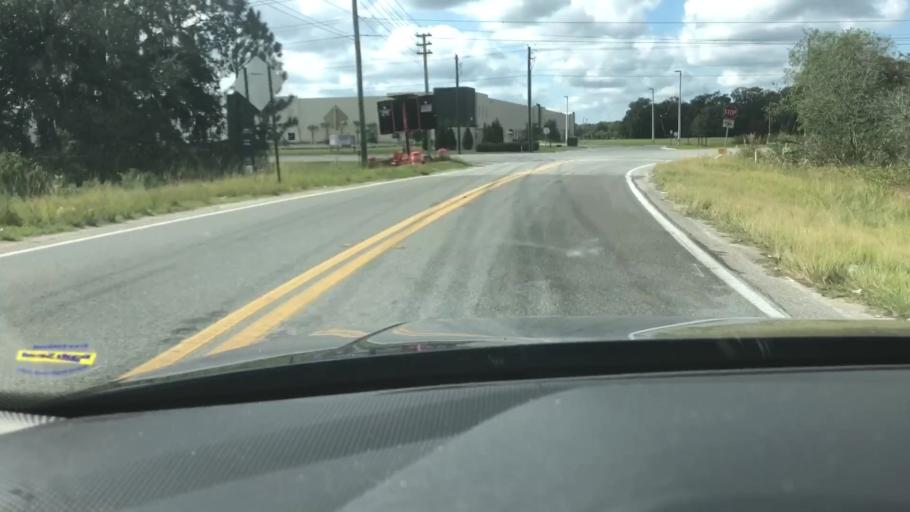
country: US
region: Florida
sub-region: Polk County
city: Winston
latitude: 28.0258
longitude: -82.0550
